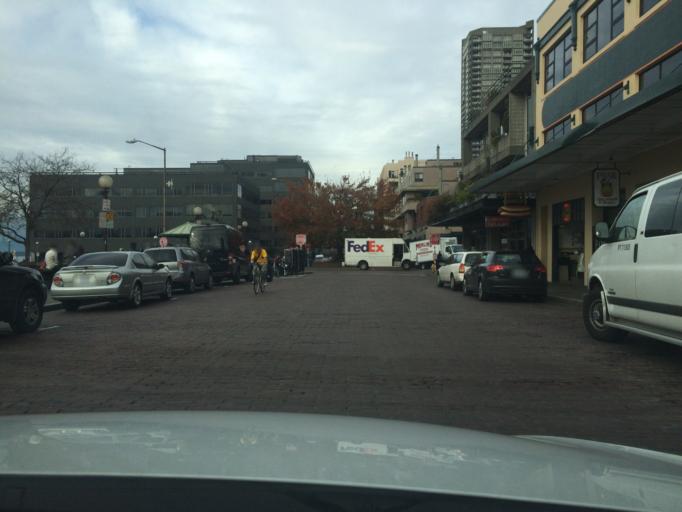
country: US
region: Washington
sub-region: King County
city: Seattle
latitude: 47.6101
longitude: -122.3429
